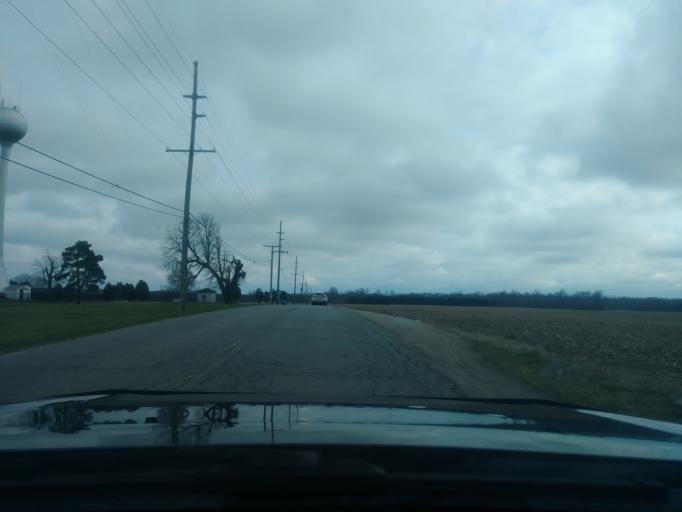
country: US
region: Indiana
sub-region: LaPorte County
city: Trail Creek
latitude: 41.6429
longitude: -86.7990
